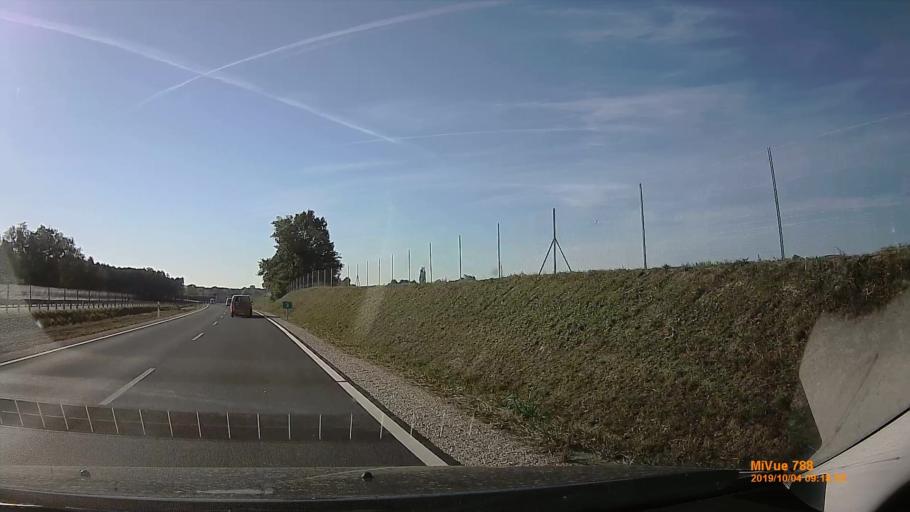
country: HU
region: Somogy
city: Karad
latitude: 46.5848
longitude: 17.8034
